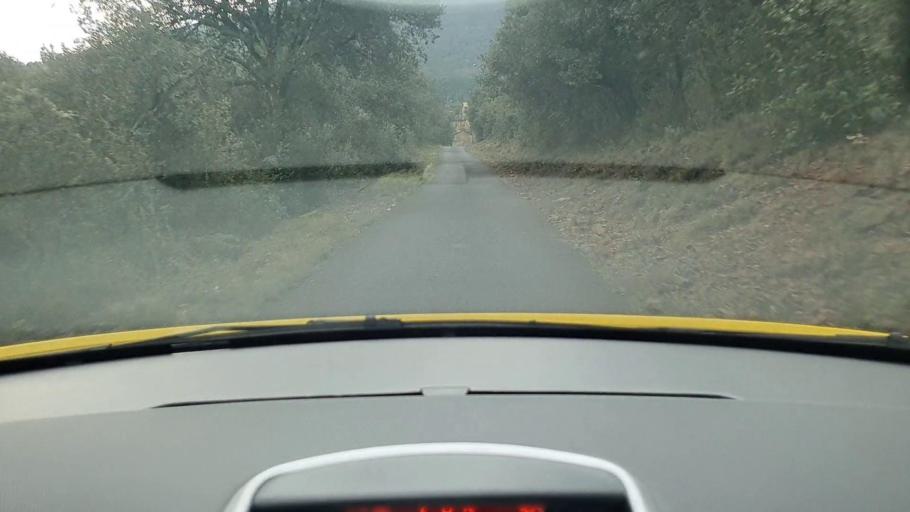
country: FR
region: Languedoc-Roussillon
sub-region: Departement du Gard
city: Saint-Florent-sur-Auzonnet
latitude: 44.2627
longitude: 4.1238
